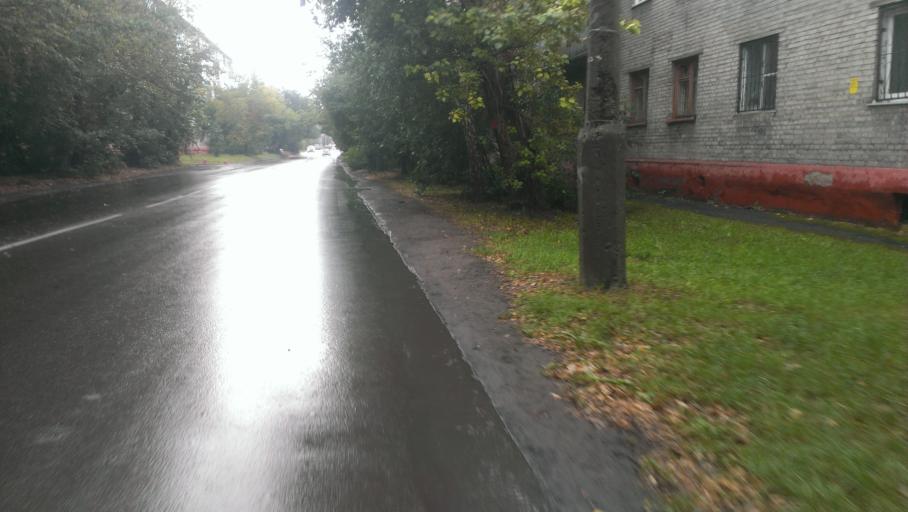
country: RU
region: Altai Krai
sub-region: Gorod Barnaulskiy
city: Barnaul
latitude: 53.3597
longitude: 83.7621
